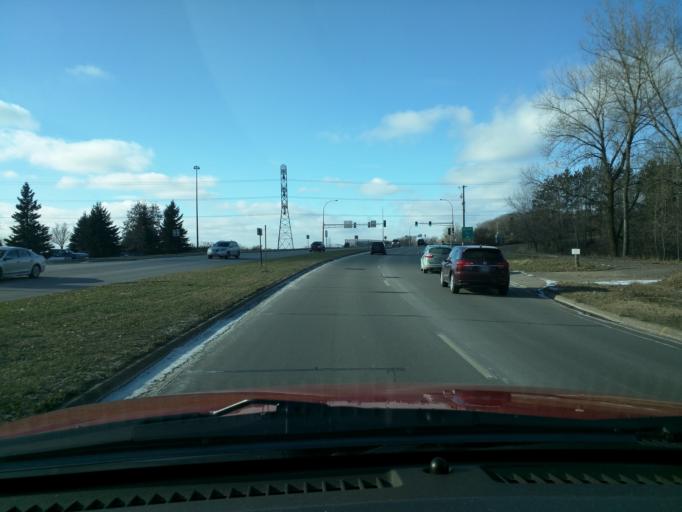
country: US
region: Minnesota
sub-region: Hennepin County
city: Eden Prairie
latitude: 44.8685
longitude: -93.4300
